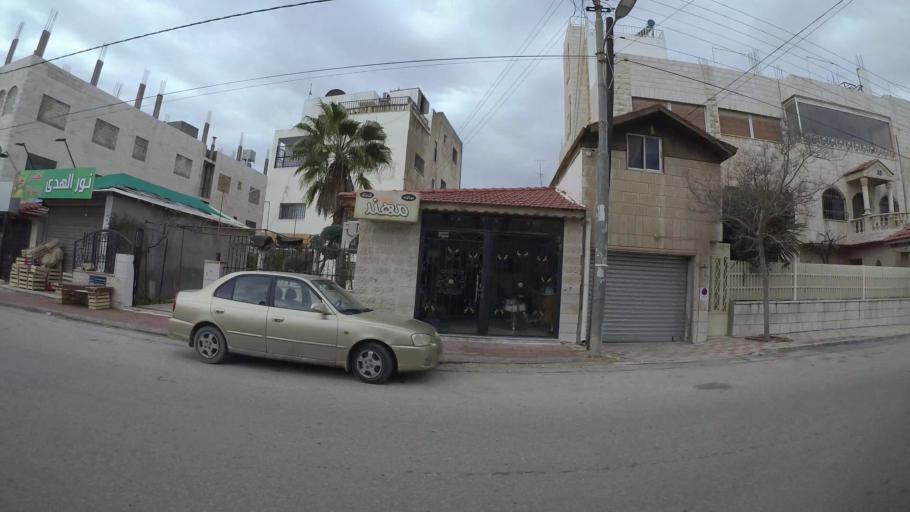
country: JO
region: Amman
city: Wadi as Sir
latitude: 31.9498
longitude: 35.8355
